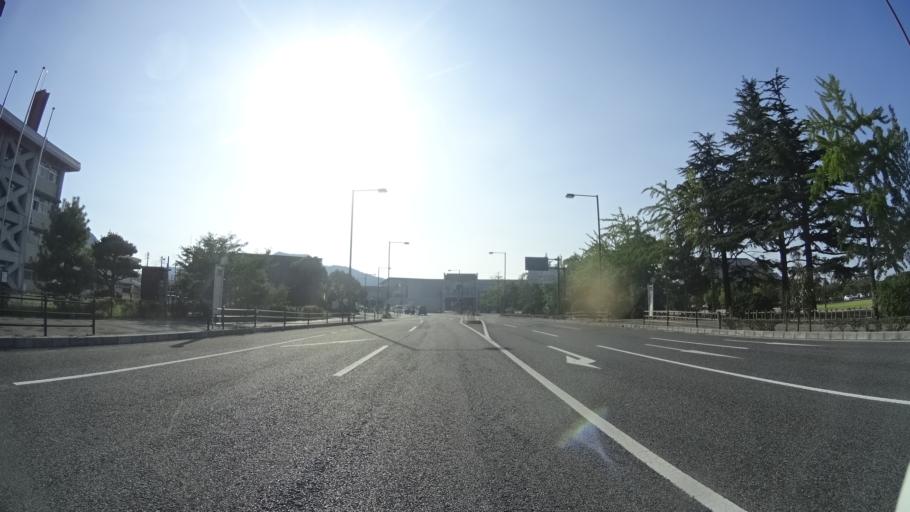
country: JP
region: Yamaguchi
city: Hagi
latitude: 34.4089
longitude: 131.3964
